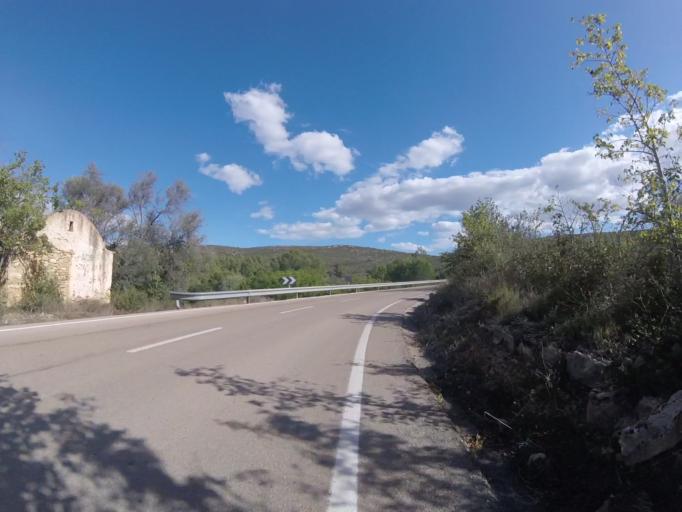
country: ES
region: Valencia
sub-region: Provincia de Castello
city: Alcala de Xivert
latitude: 40.2952
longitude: 0.1766
